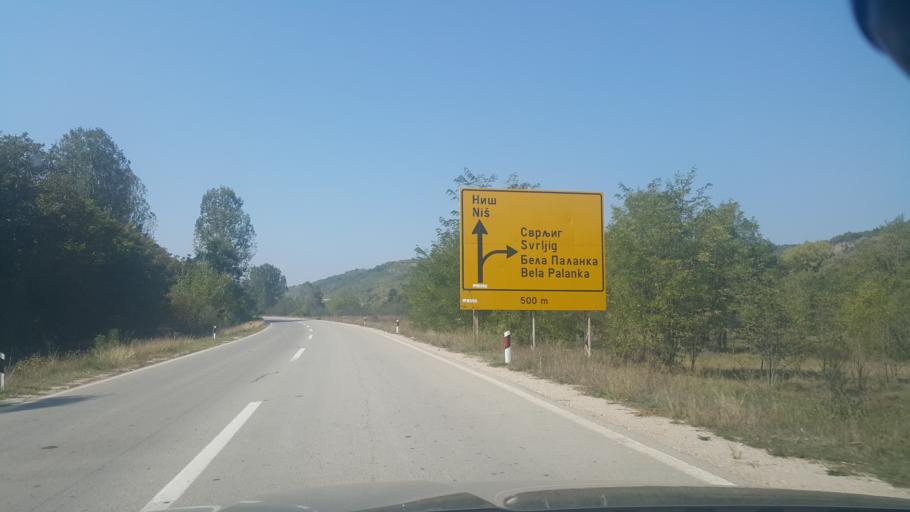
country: RS
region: Central Serbia
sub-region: Pirotski Okrug
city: Bela Palanka
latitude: 43.2300
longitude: 22.3247
